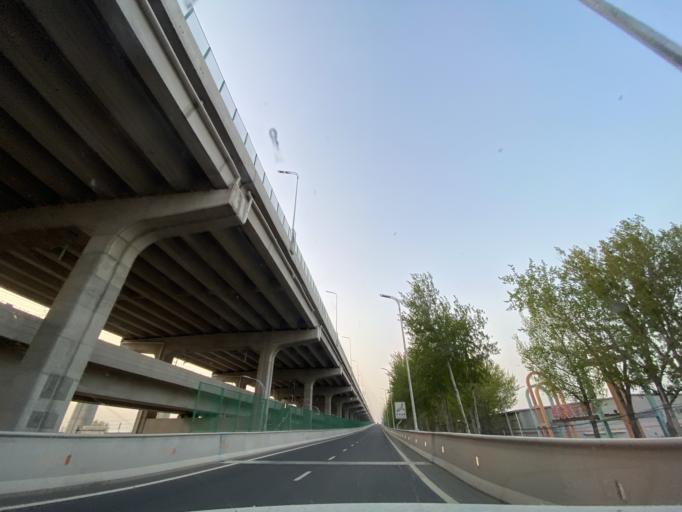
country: CN
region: Beijing
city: Weishanzhuang
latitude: 39.6169
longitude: 116.3789
